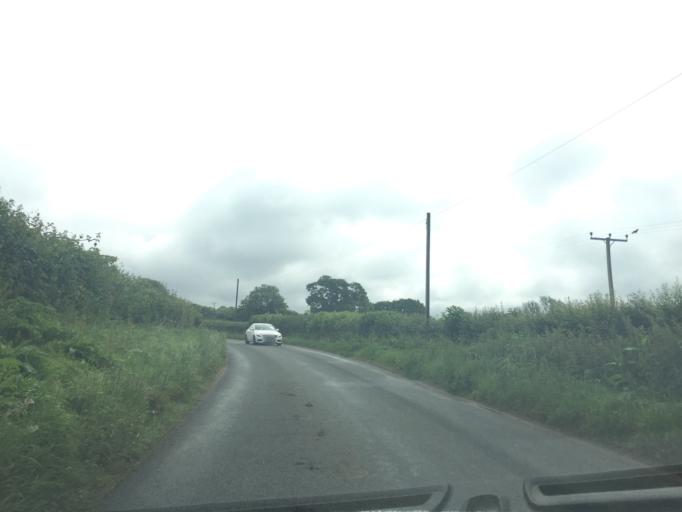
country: GB
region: England
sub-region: Dorset
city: Bovington Camp
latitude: 50.7192
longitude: -2.2961
